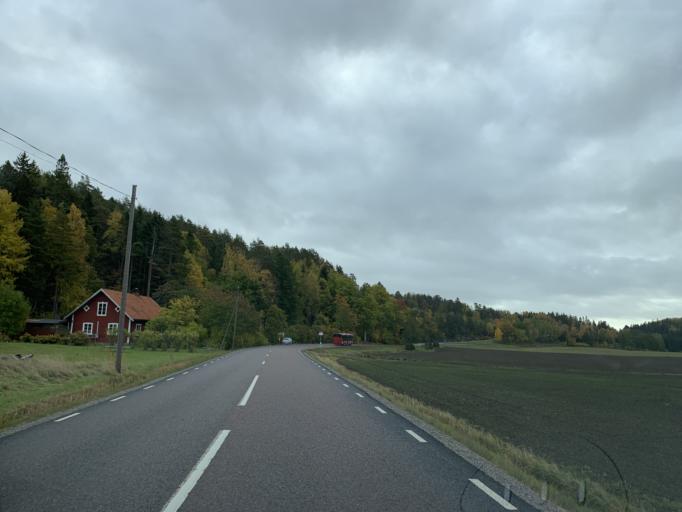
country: SE
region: Stockholm
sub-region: Nynashamns Kommun
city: Osmo
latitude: 58.9751
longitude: 17.7757
